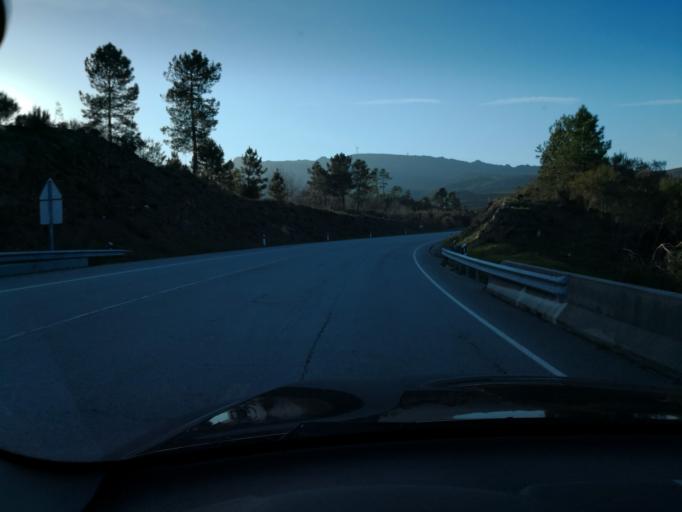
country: PT
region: Vila Real
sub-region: Vila Real
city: Vila Real
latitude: 41.3730
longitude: -7.7133
